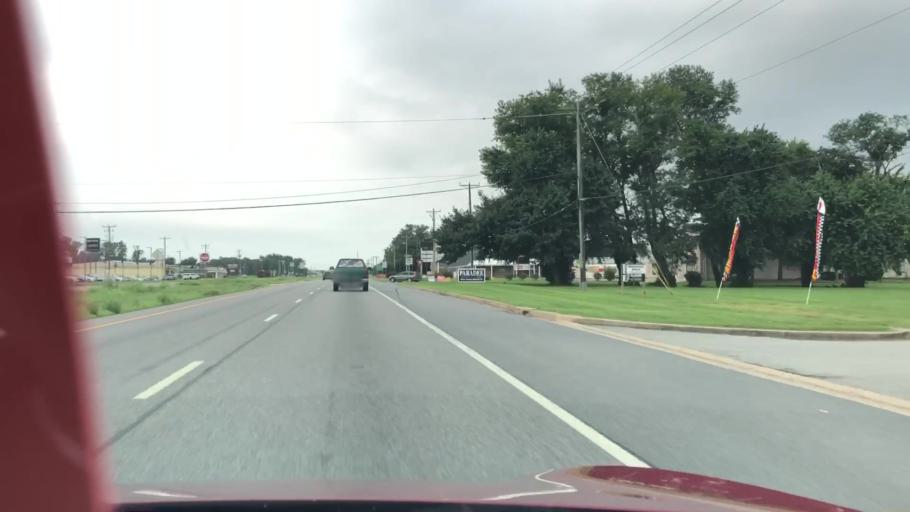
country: US
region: Delaware
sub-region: Kent County
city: Camden
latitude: 39.1194
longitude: -75.5347
